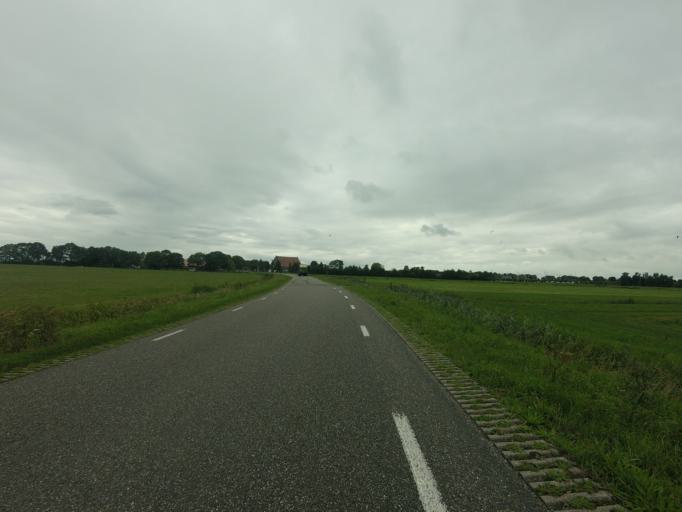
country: NL
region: Friesland
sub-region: Sudwest Fryslan
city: Heeg
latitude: 52.9693
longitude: 5.5467
